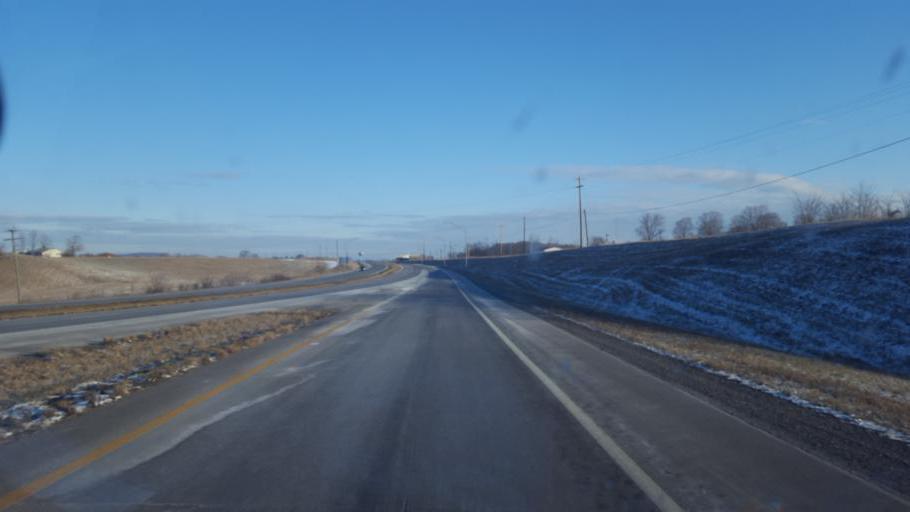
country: US
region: Ohio
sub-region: Pike County
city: Piketon
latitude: 39.0499
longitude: -83.0219
